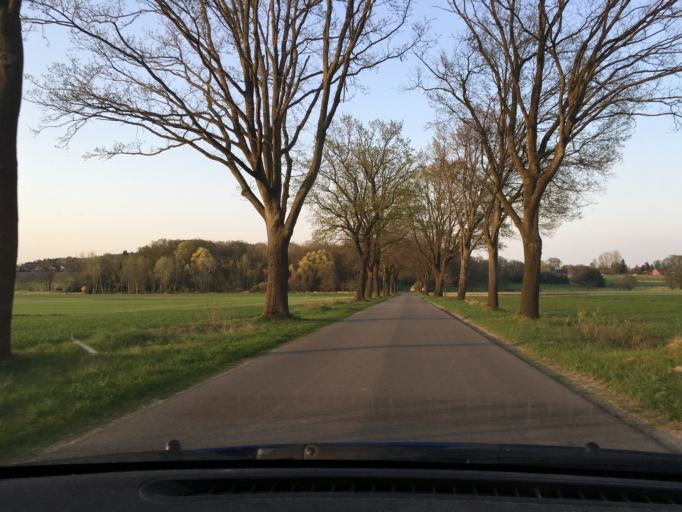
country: DE
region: Lower Saxony
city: Sudergellersen
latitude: 53.2017
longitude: 10.2883
